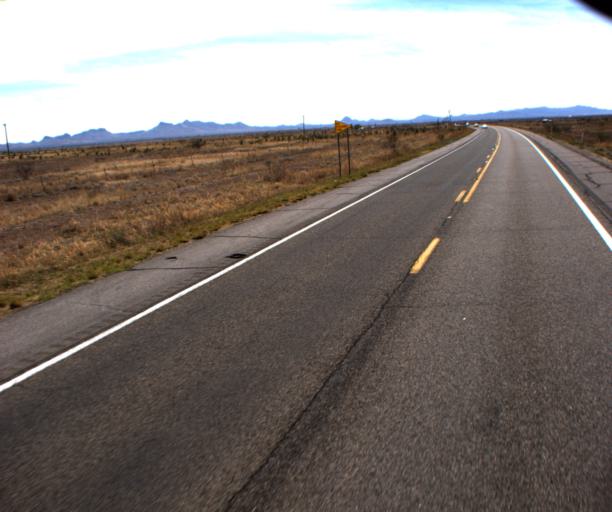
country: US
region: Arizona
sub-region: Cochise County
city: Pirtleville
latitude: 31.4553
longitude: -109.6101
